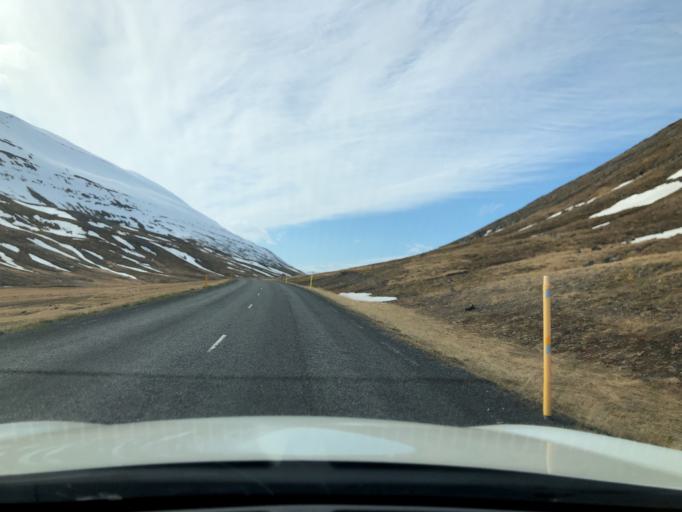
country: IS
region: East
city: Egilsstadir
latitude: 65.1737
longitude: -14.3402
